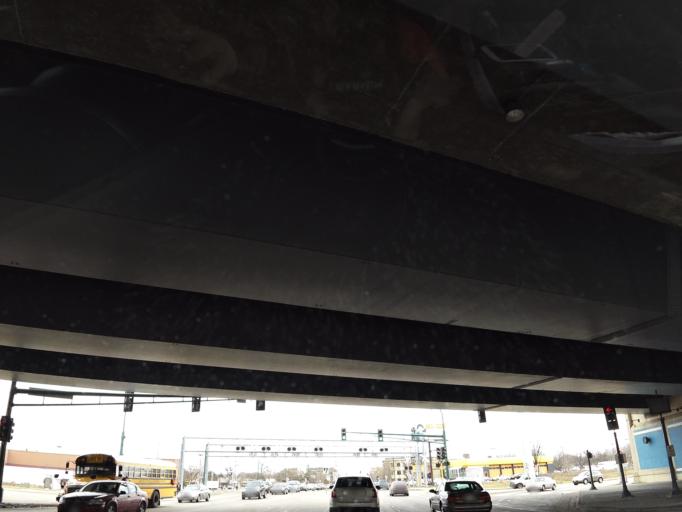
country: US
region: Minnesota
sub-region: Hennepin County
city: Minneapolis
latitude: 44.9484
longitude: -93.2384
